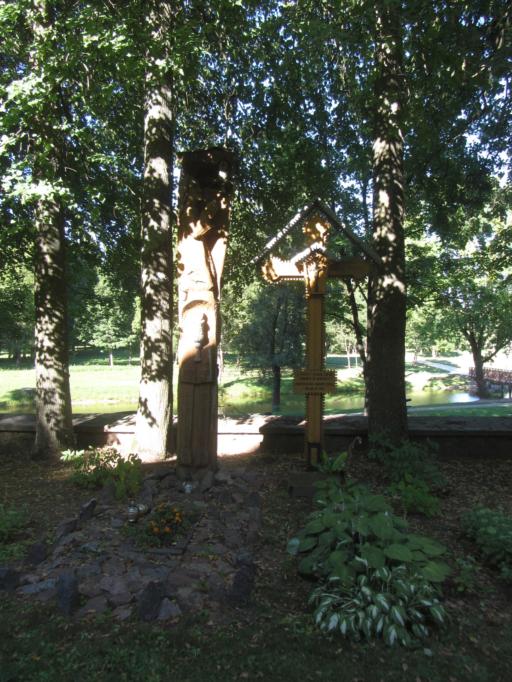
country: LT
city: Obeliai
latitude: 55.7488
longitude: 25.3053
